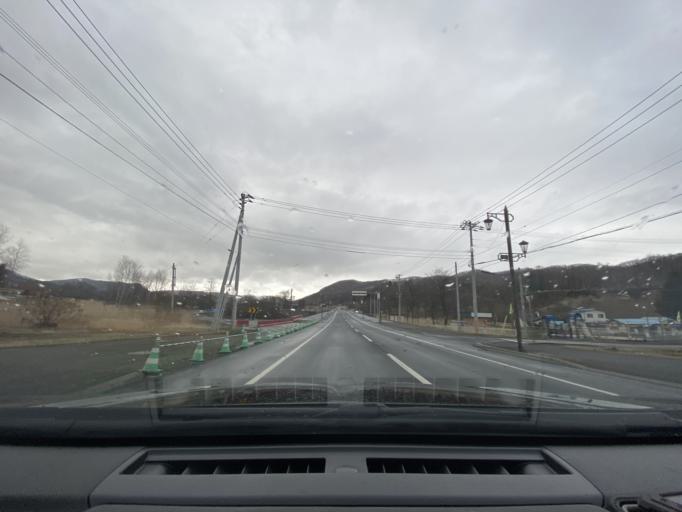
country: JP
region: Hokkaido
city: Otofuke
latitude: 43.2524
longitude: 143.5476
